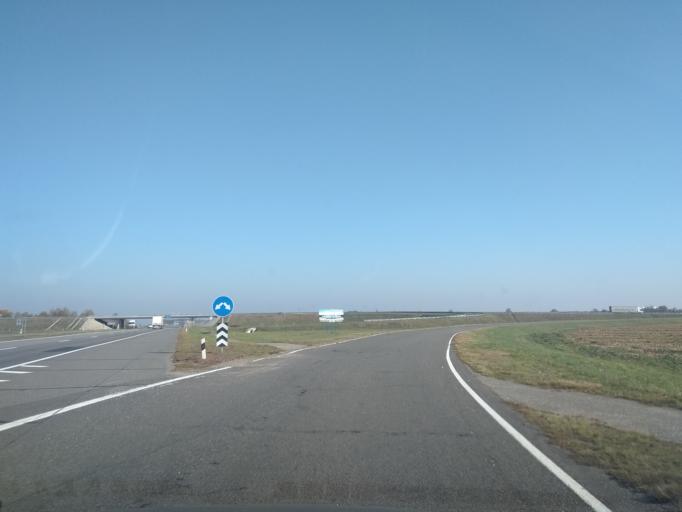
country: BY
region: Brest
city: Ivatsevichy
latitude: 52.6974
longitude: 25.3588
